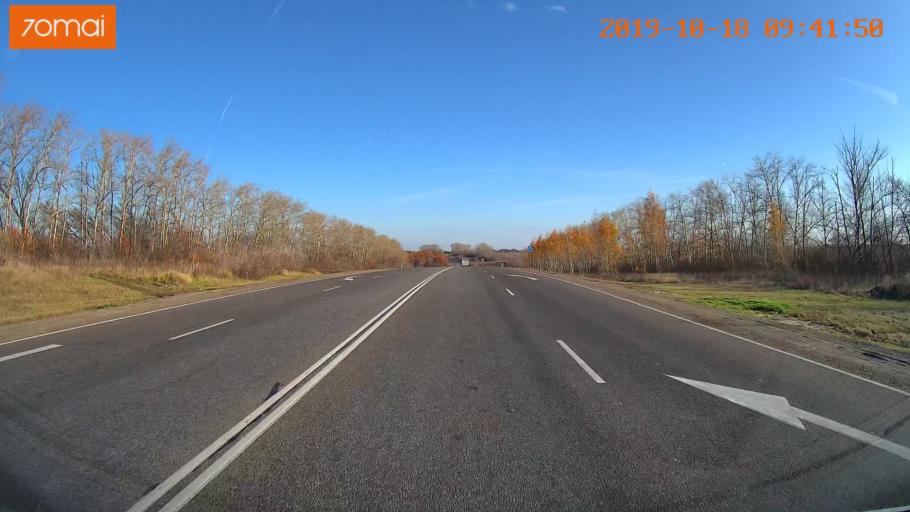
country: RU
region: Tula
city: Kazachka
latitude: 53.2796
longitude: 38.1677
